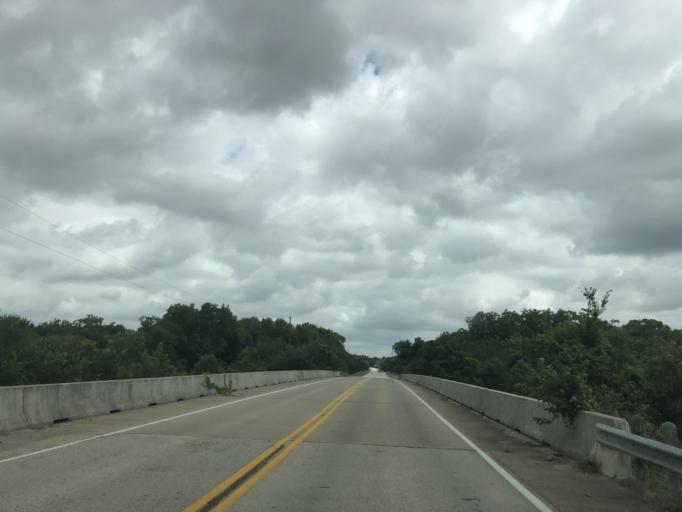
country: US
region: Texas
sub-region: Dallas County
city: Sunnyvale
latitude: 32.8172
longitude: -96.5595
